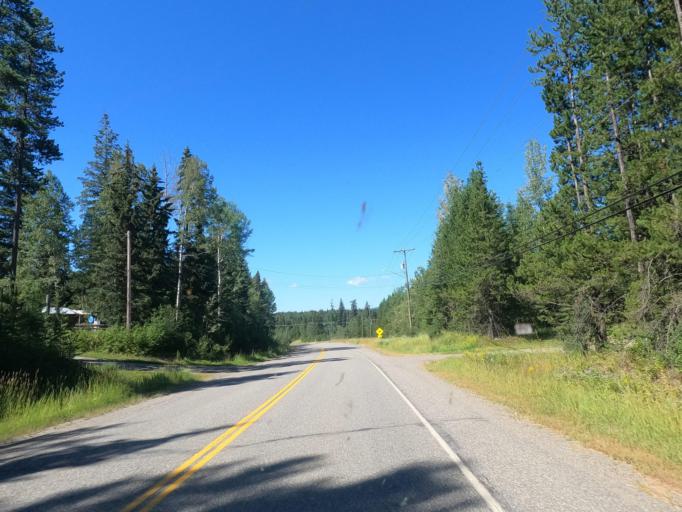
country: CA
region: British Columbia
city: Quesnel
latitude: 53.0324
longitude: -122.4058
